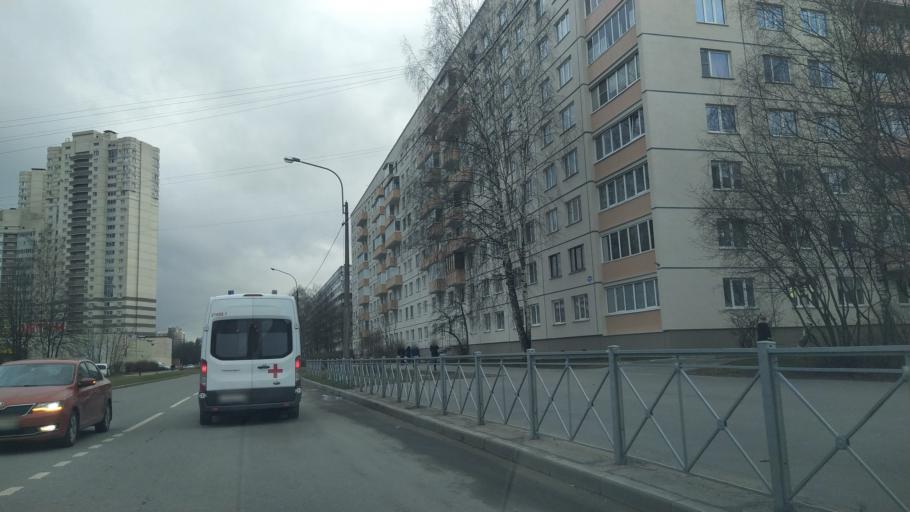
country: RU
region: St.-Petersburg
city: Grazhdanka
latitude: 60.0381
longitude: 30.4056
